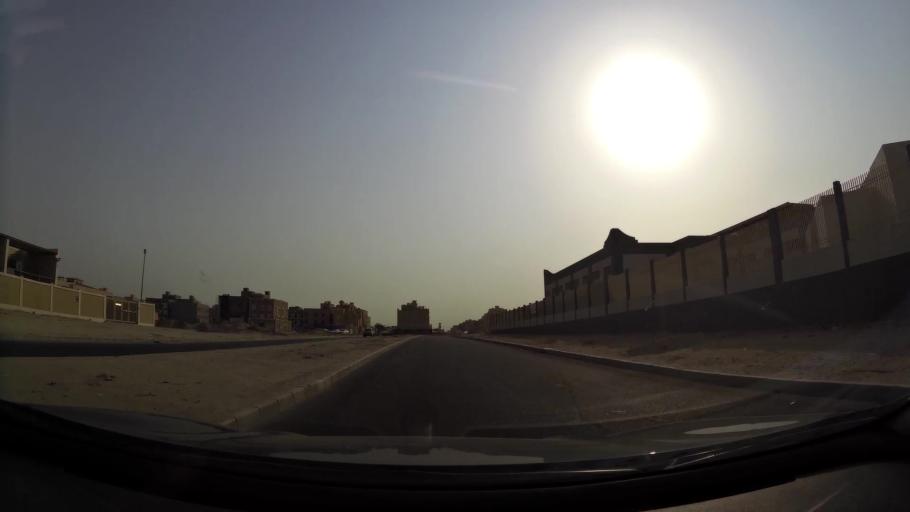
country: KW
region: Al Asimah
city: Ar Rabiyah
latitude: 29.3282
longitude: 47.8007
